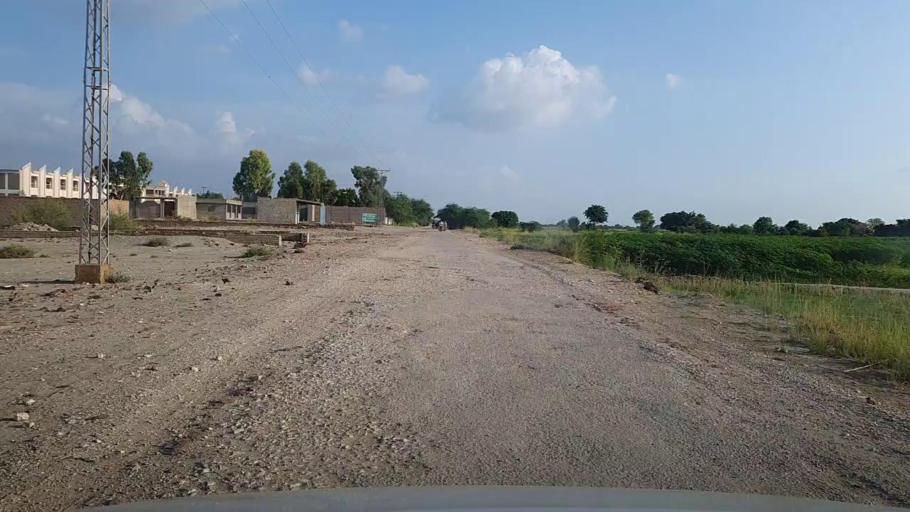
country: PK
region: Sindh
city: Hingorja
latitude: 27.0834
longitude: 68.4188
